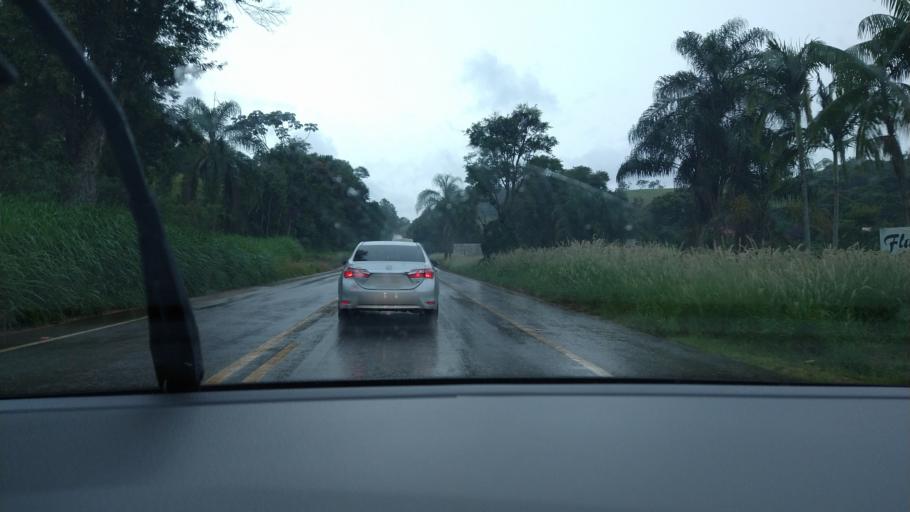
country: BR
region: Minas Gerais
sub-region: Vicosa
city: Vicosa
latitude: -20.6253
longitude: -42.8700
